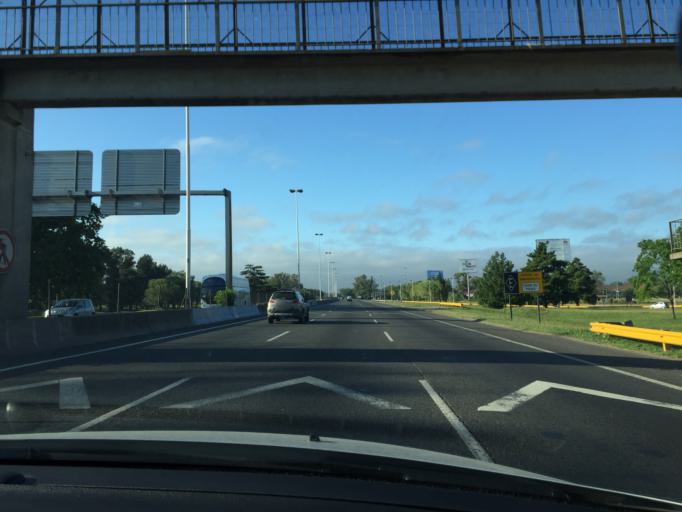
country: AR
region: Buenos Aires
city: San Justo
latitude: -34.7342
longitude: -58.5185
